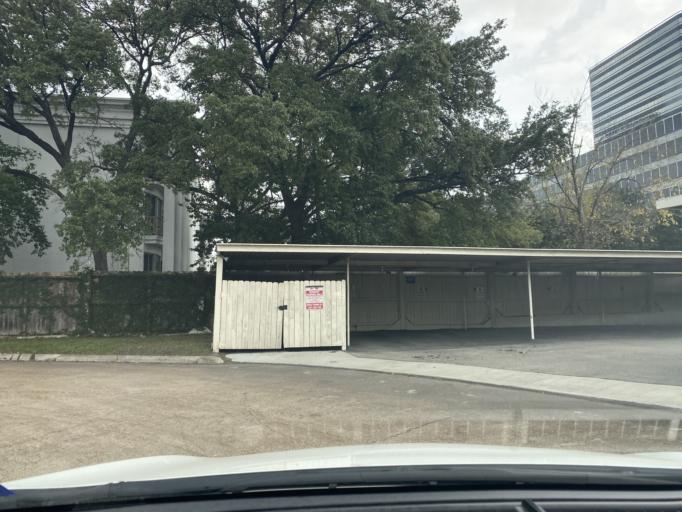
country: US
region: Texas
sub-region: Harris County
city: Hunters Creek Village
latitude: 29.7468
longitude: -95.4644
